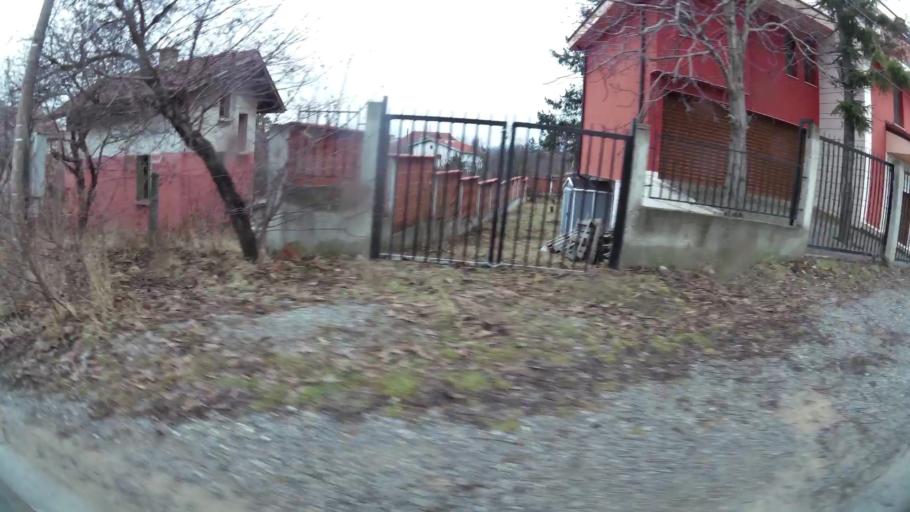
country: BG
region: Sofia-Capital
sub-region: Stolichna Obshtina
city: Sofia
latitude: 42.6177
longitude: 23.3700
